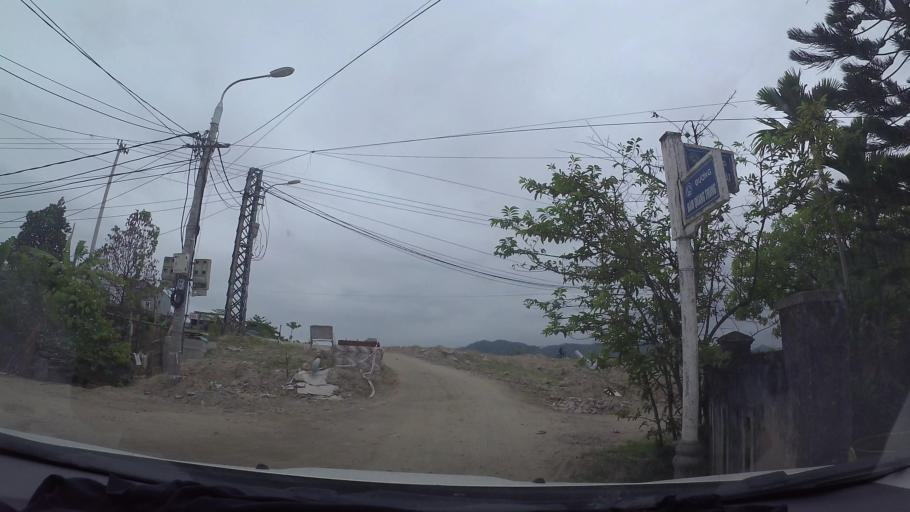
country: VN
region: Da Nang
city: Lien Chieu
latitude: 16.1028
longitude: 108.1299
